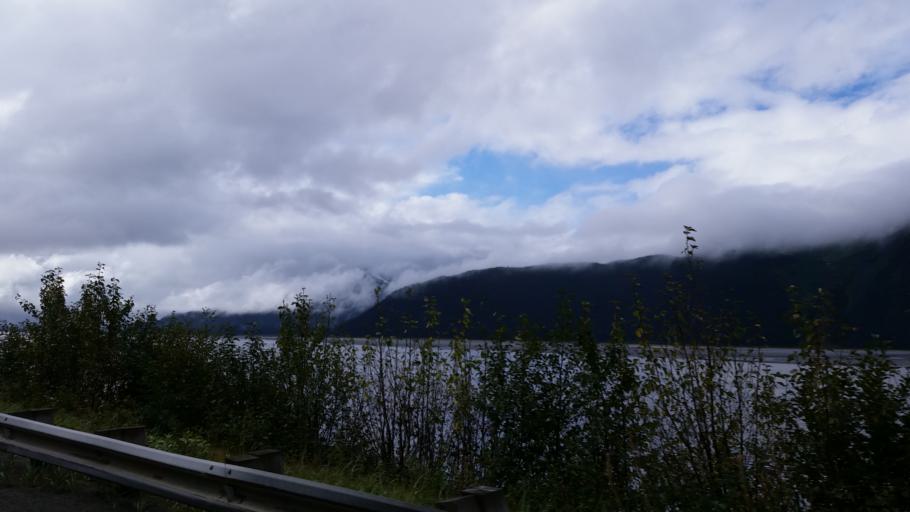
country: US
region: Alaska
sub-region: Anchorage Municipality
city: Girdwood
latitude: 60.8926
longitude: -149.0637
